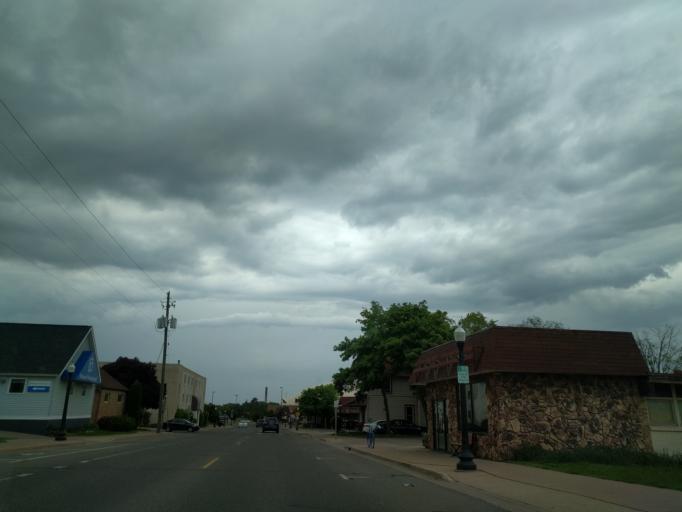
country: US
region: Michigan
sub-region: Marquette County
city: Marquette
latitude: 46.5549
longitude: -87.3948
